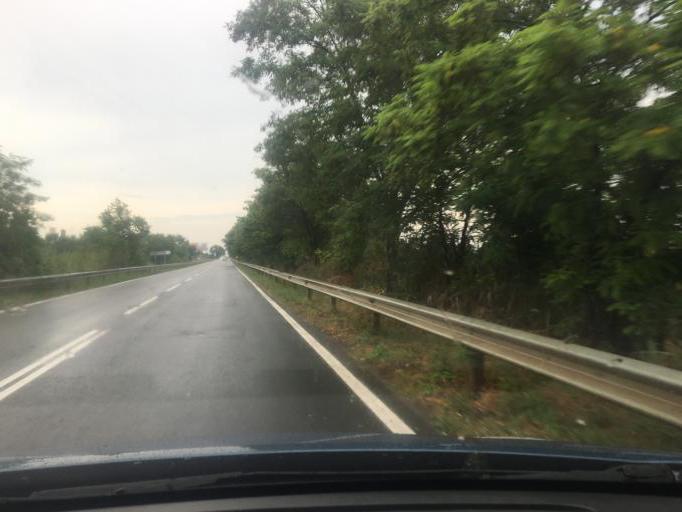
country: BG
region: Burgas
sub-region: Obshtina Pomorie
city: Pomorie
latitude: 42.5668
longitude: 27.6034
